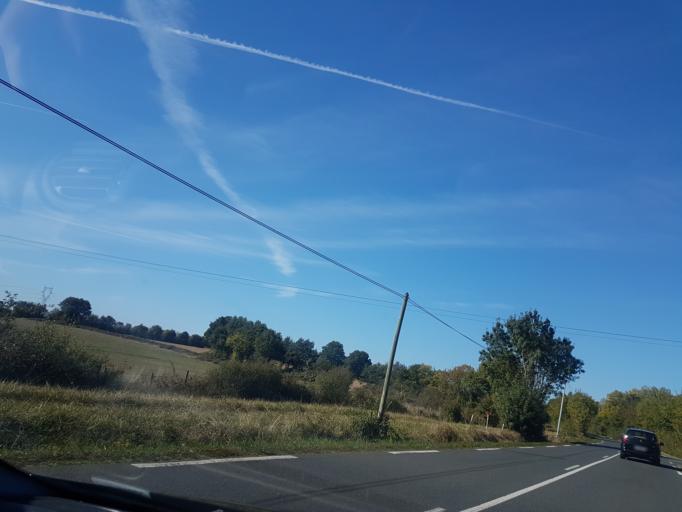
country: FR
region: Pays de la Loire
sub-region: Departement de la Loire-Atlantique
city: Casson
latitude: 47.4285
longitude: -1.5612
